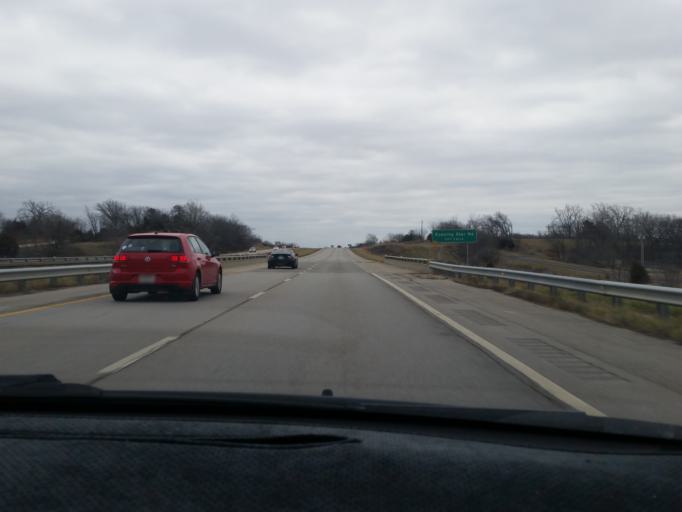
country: US
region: Kansas
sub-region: Douglas County
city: Eudora
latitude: 38.9429
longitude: -95.0602
